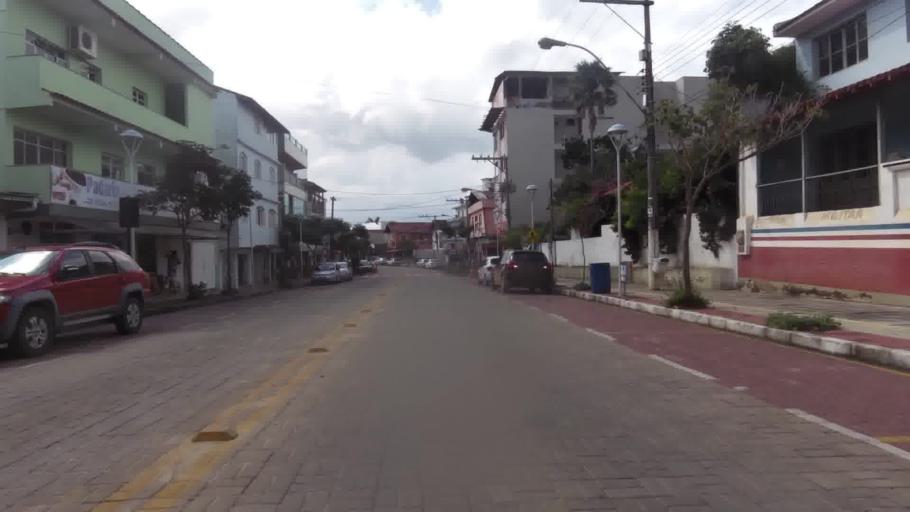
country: BR
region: Espirito Santo
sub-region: Piuma
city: Piuma
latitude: -20.8320
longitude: -40.6958
